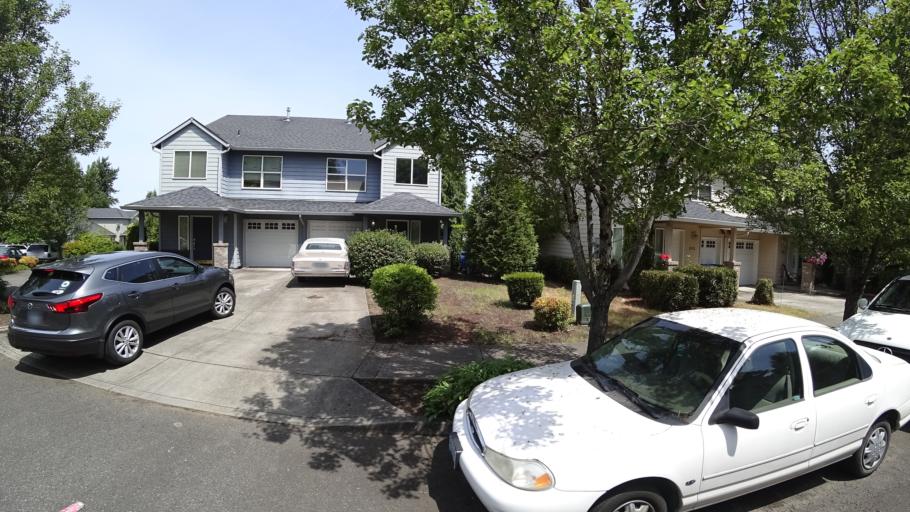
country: US
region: Oregon
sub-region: Multnomah County
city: Fairview
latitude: 45.5485
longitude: -122.5020
